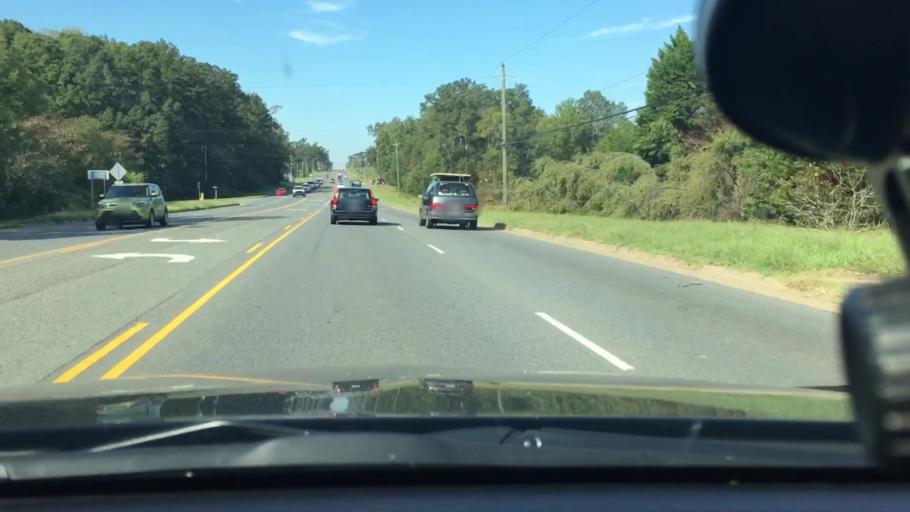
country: US
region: North Carolina
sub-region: Cabarrus County
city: Midland
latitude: 35.2497
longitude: -80.5281
